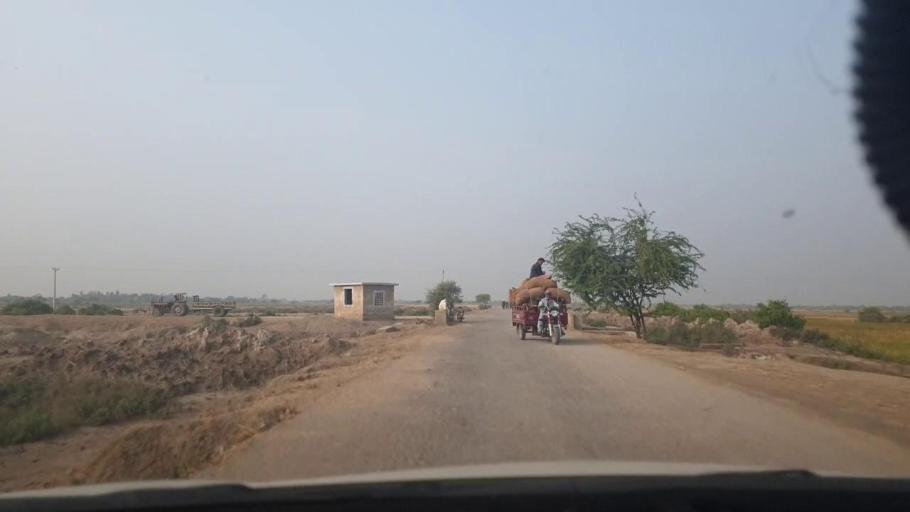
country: PK
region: Sindh
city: Bulri
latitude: 24.7864
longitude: 68.4193
